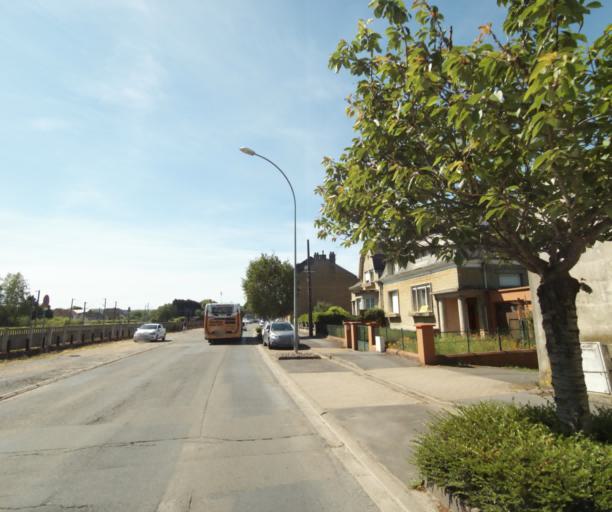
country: FR
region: Champagne-Ardenne
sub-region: Departement des Ardennes
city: Villers-Semeuse
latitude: 49.7483
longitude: 4.7364
